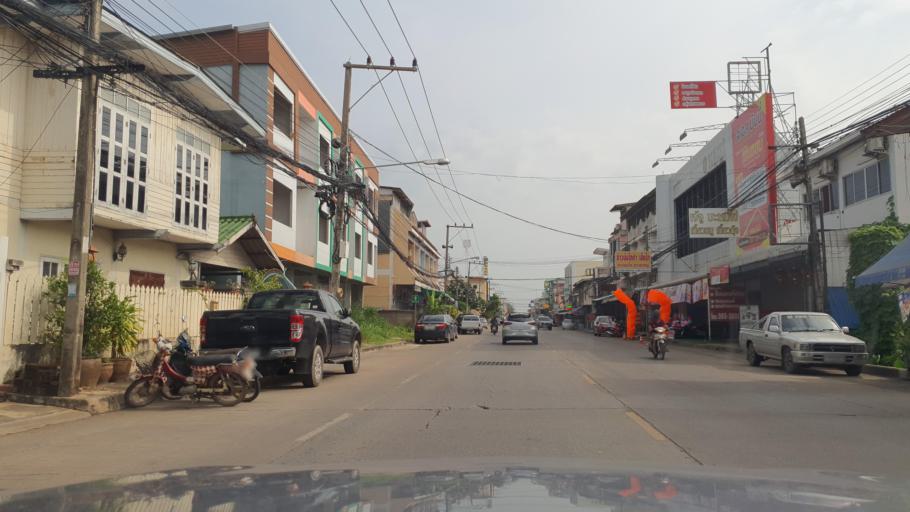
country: TH
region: Phitsanulok
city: Phitsanulok
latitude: 16.8306
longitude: 100.2655
